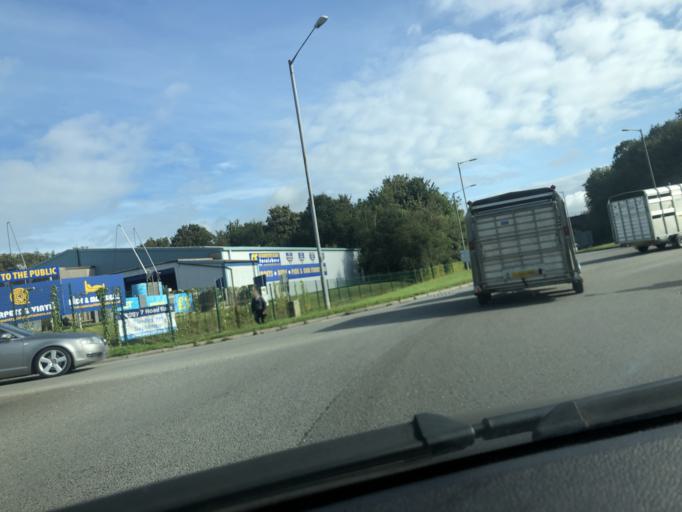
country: GB
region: England
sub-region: Cornwall
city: Launceston
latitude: 50.6276
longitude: -4.3703
